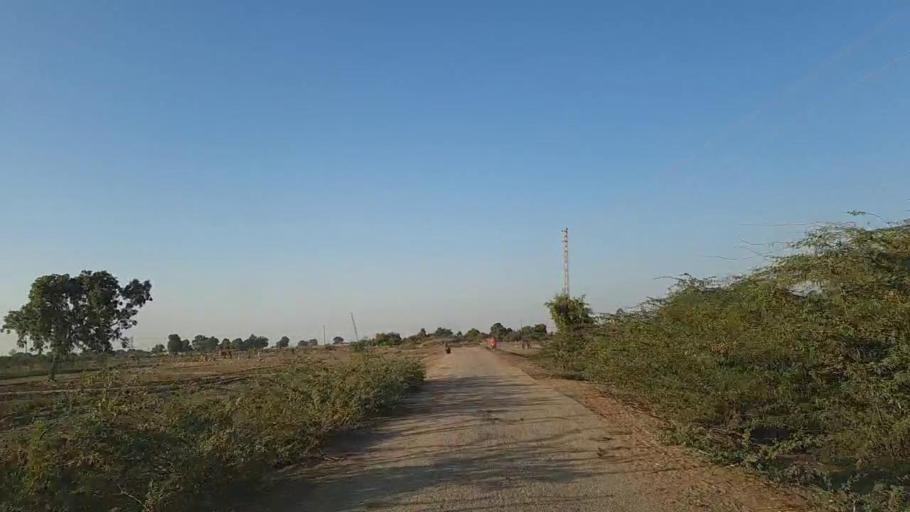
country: PK
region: Sindh
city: Naukot
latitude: 25.0009
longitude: 69.3910
